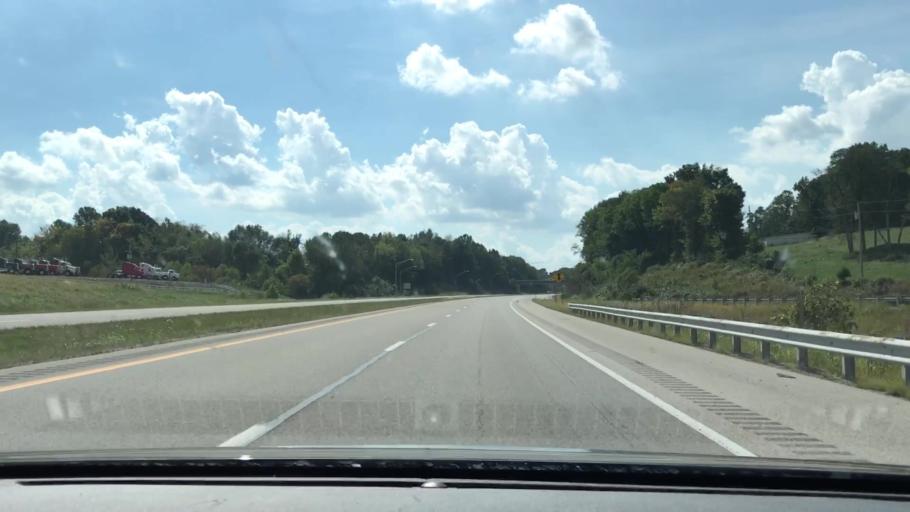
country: US
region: Kentucky
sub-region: Barren County
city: Glasgow
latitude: 36.9822
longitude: -85.8960
